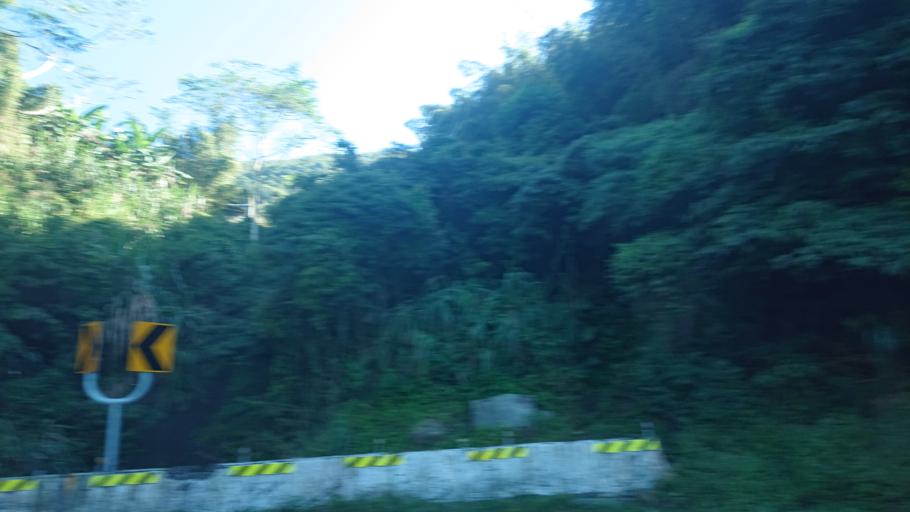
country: TW
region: Taiwan
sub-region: Chiayi
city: Jiayi Shi
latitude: 23.5234
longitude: 120.6328
